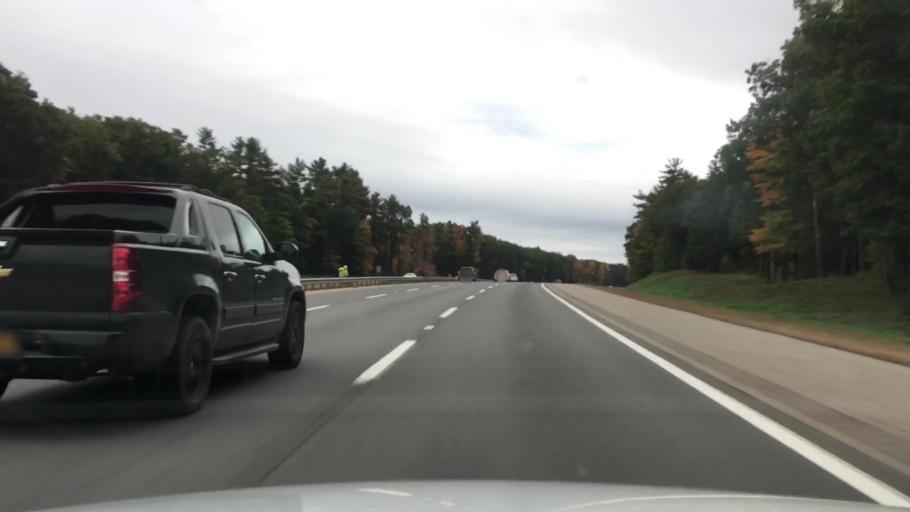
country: US
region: Maine
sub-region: York County
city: Ogunquit
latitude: 43.2576
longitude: -70.6203
